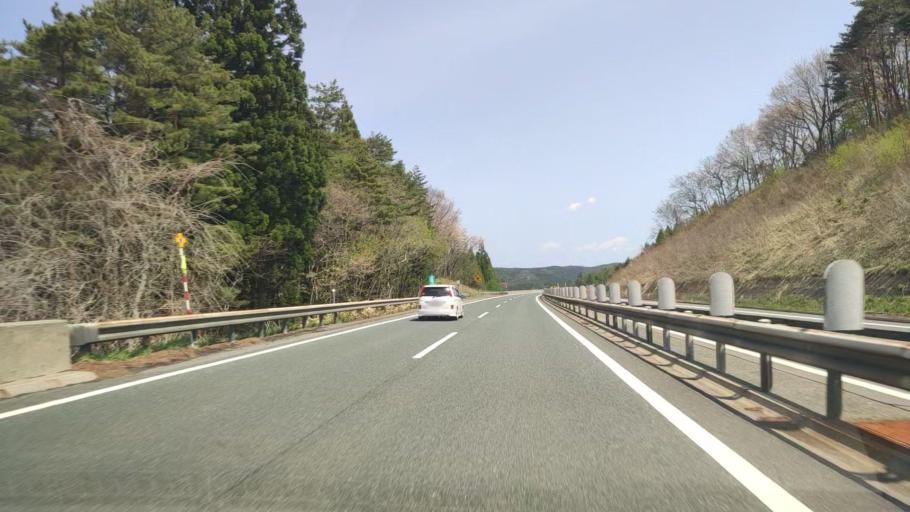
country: JP
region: Iwate
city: Ichinohe
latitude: 40.1543
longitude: 141.1196
